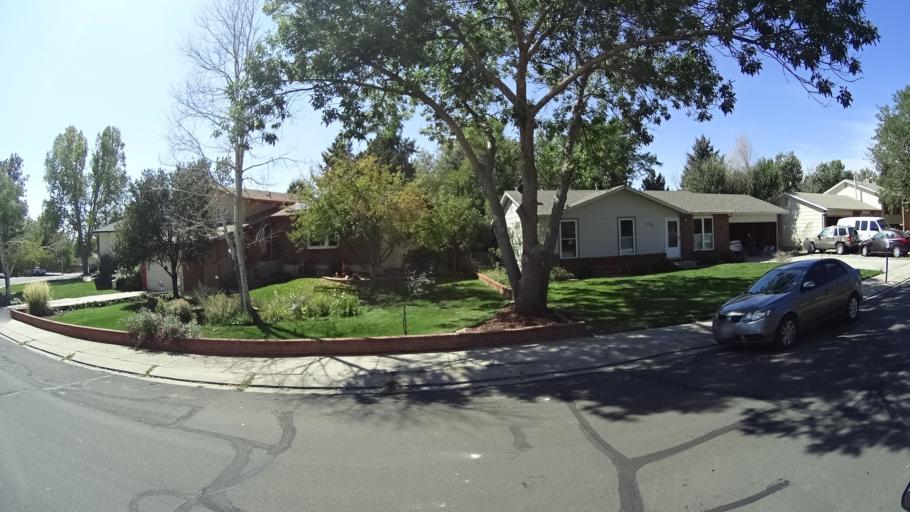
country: US
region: Colorado
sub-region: El Paso County
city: Cimarron Hills
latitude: 38.9056
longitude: -104.7605
